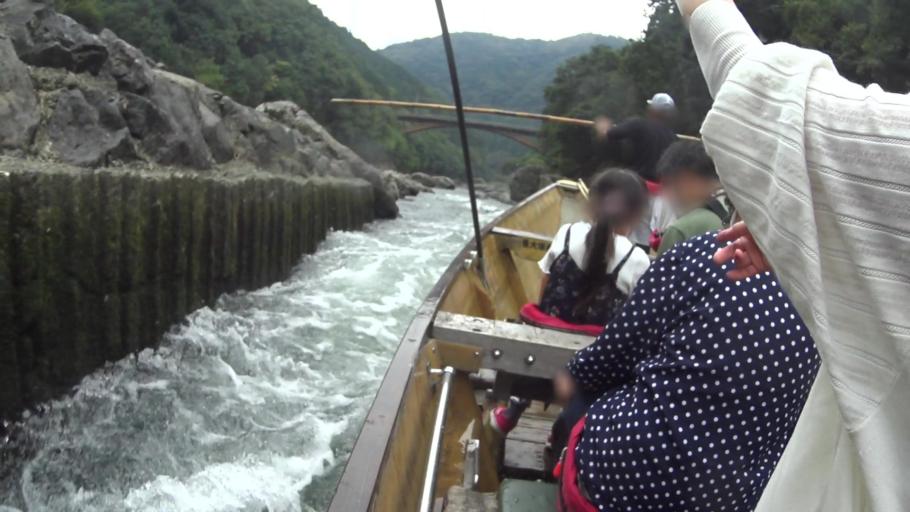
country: JP
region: Kyoto
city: Kameoka
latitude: 35.0232
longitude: 135.6210
